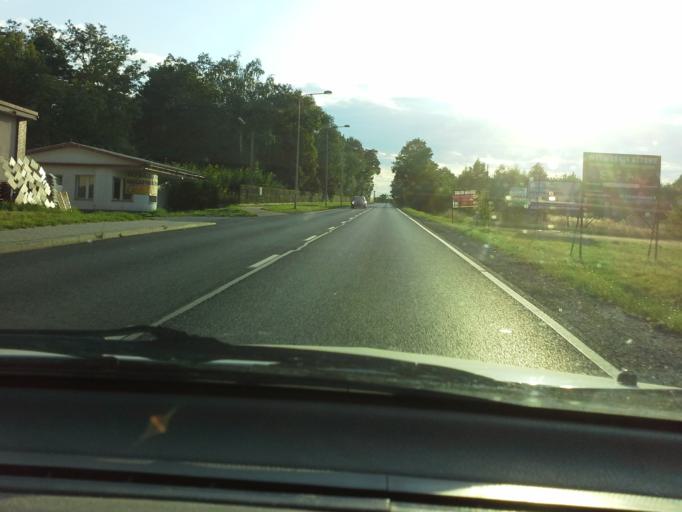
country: PL
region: Lesser Poland Voivodeship
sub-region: Powiat krakowski
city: Tenczynek
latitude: 50.1311
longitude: 19.6154
